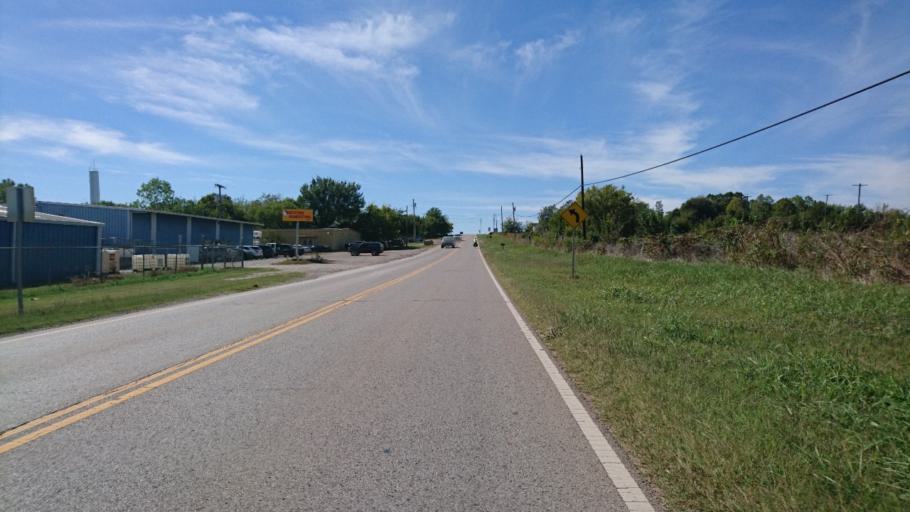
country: US
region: Oklahoma
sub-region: Lincoln County
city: Stroud
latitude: 35.7510
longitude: -96.6772
